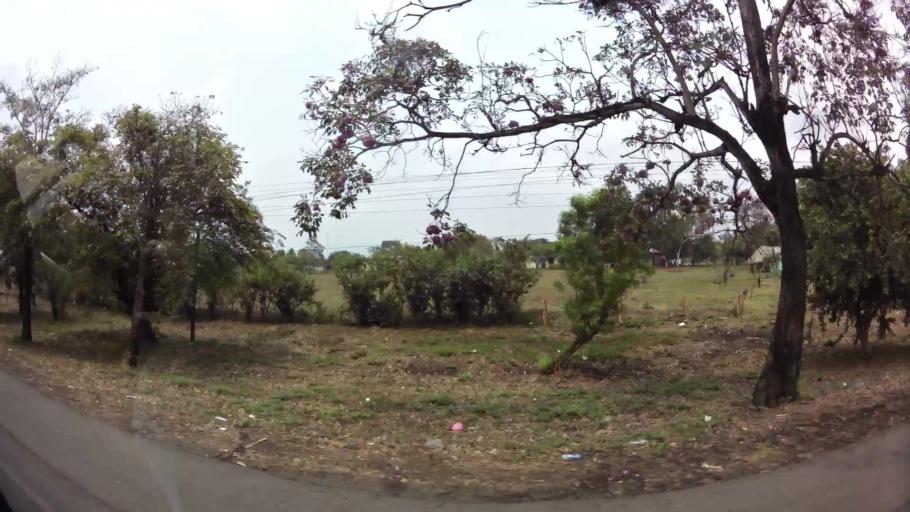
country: NI
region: Chinandega
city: Chinandega
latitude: 12.6424
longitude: -87.1291
